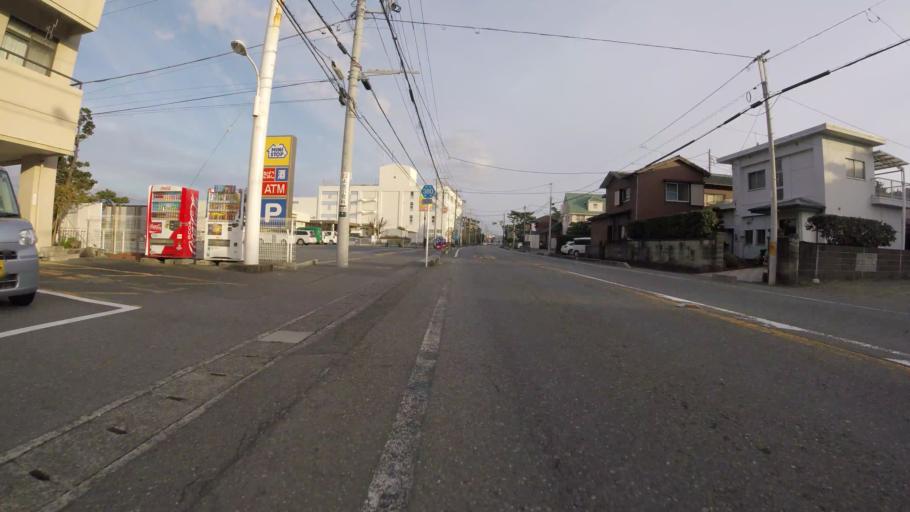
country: JP
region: Shizuoka
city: Numazu
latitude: 35.1223
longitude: 138.7989
